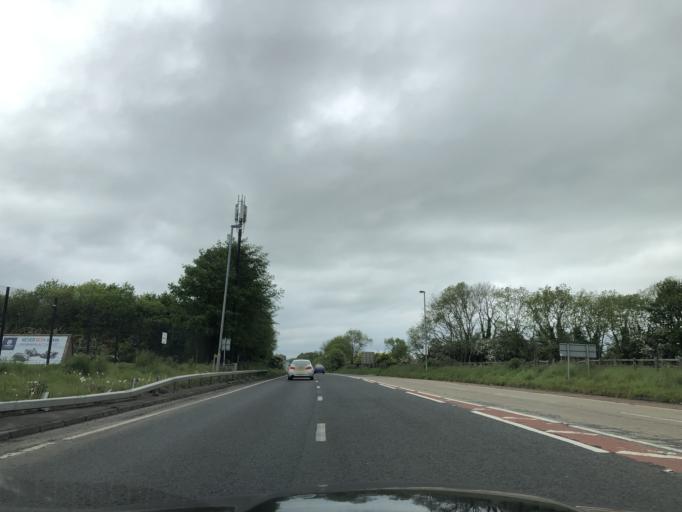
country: GB
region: Northern Ireland
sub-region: Antrim Borough
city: Crumlin
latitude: 54.6359
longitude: -6.1484
